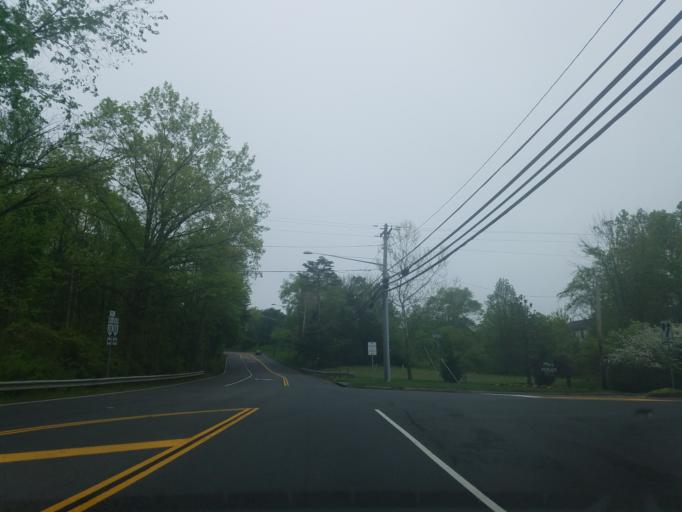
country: US
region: Virginia
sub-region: Fairfax County
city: Centreville
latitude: 38.8479
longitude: -77.4383
